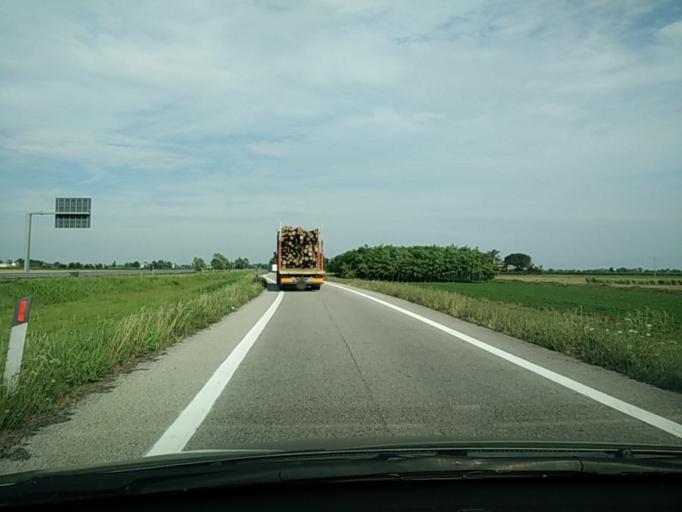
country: IT
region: Veneto
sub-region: Provincia di Venezia
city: Fossalta di Piave
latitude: 45.6117
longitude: 12.4953
